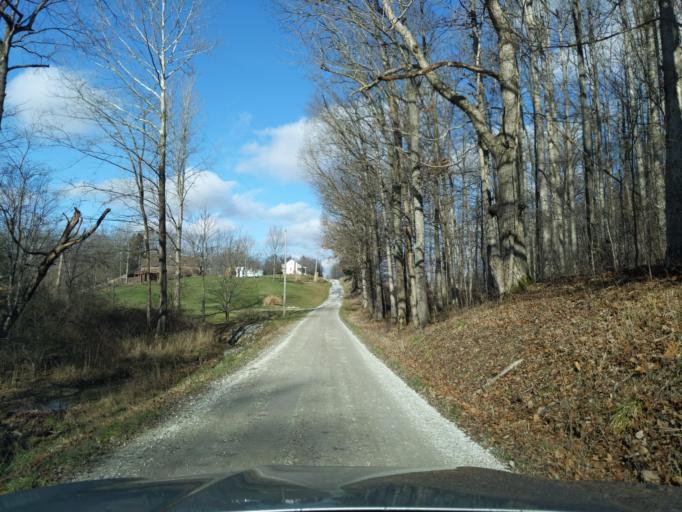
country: US
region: Indiana
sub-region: Decatur County
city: Greensburg
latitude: 39.2530
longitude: -85.4842
